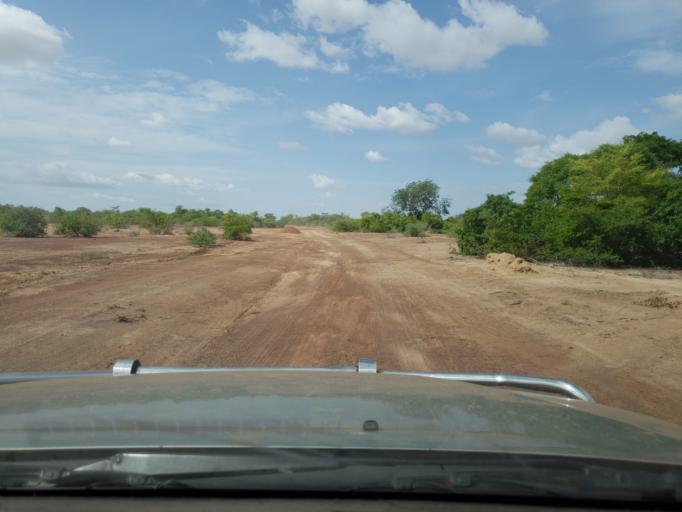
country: ML
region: Segou
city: Bla
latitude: 12.7760
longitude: -5.6114
